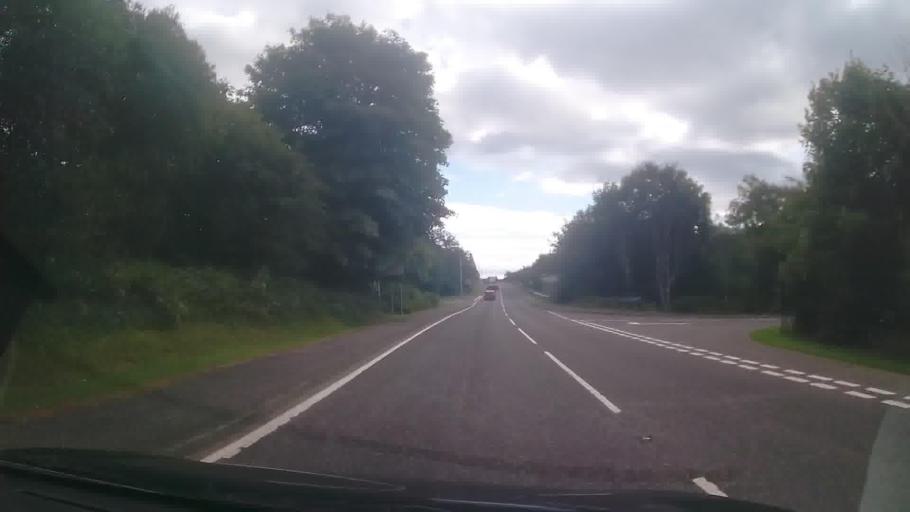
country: GB
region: Scotland
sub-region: Argyll and Bute
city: Oban
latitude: 56.4597
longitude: -5.3923
